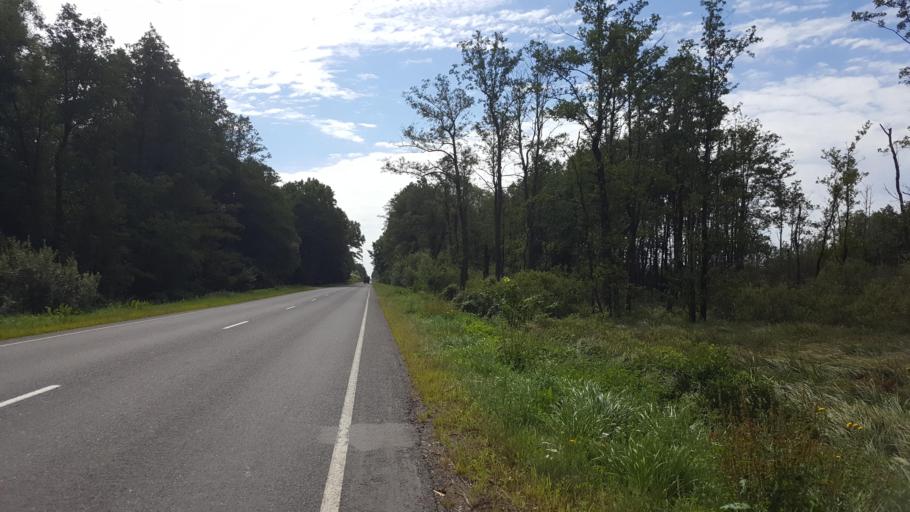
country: BY
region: Brest
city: Zhabinka
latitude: 52.2801
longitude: 23.9487
